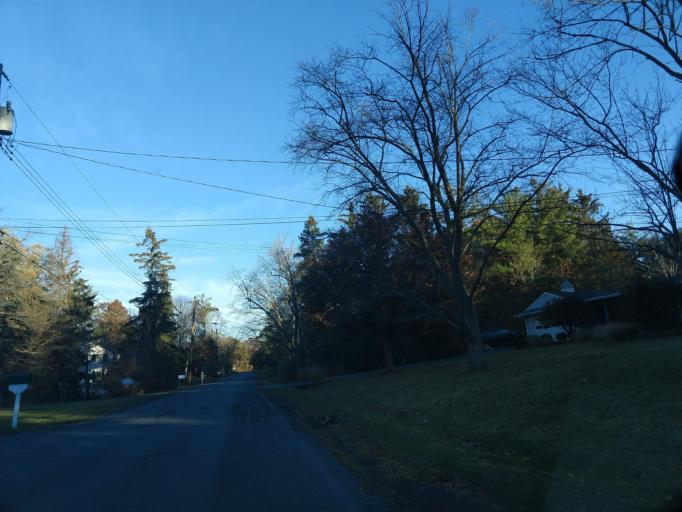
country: US
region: New York
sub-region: Tompkins County
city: Cayuga Heights
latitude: 42.4673
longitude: -76.4850
